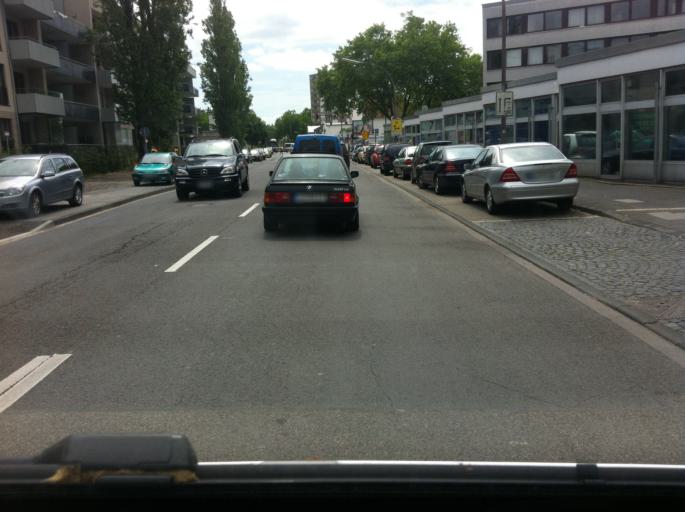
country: DE
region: North Rhine-Westphalia
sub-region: Regierungsbezirk Koln
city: Neuehrenfeld
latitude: 50.9439
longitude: 6.9081
